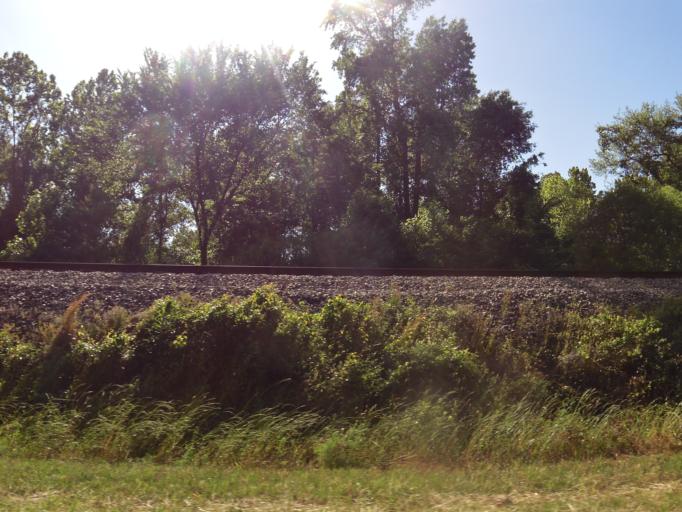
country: US
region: South Carolina
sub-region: Allendale County
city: Fairfax
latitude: 33.0337
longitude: -81.2227
